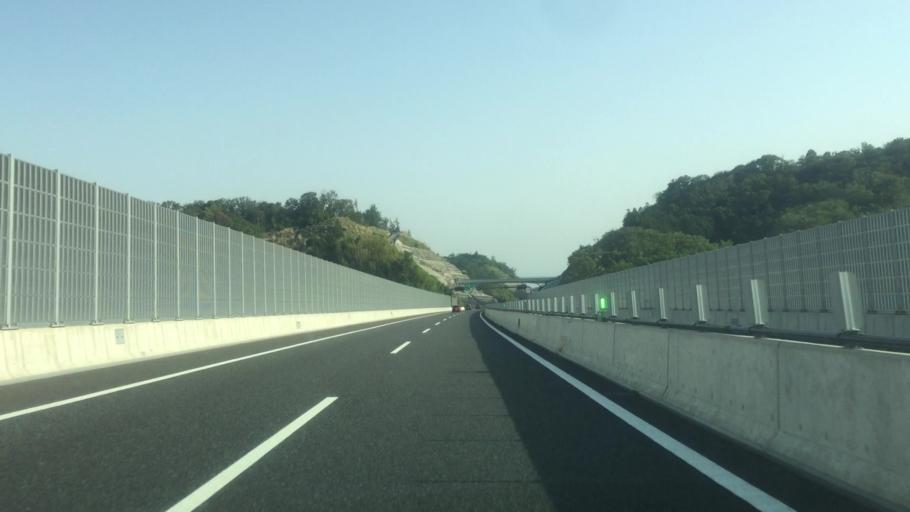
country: JP
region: Aichi
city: Okazaki
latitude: 35.0100
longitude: 137.2278
